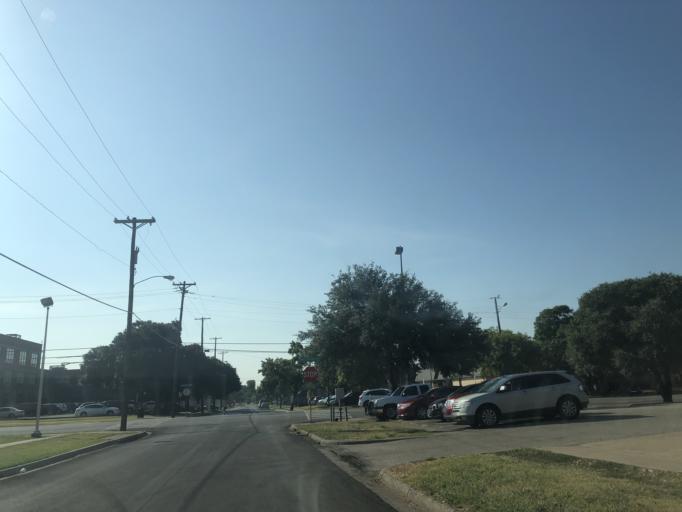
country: US
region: Texas
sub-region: Dallas County
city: Dallas
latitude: 32.7716
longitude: -96.7666
